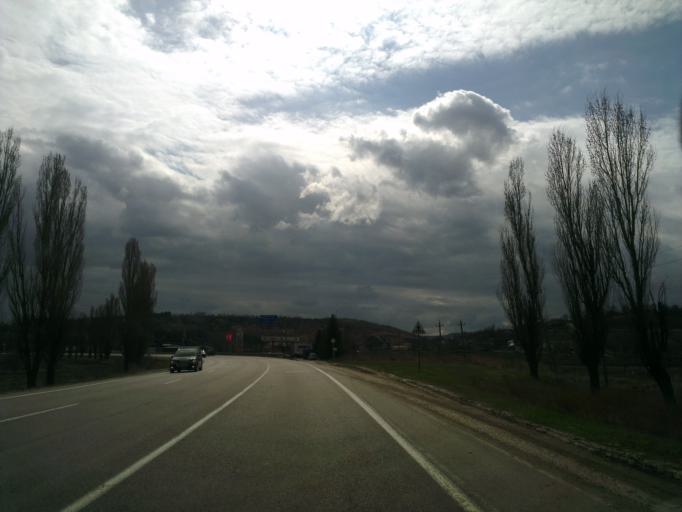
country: MD
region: Laloveni
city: Ialoveni
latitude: 46.9133
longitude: 28.6885
